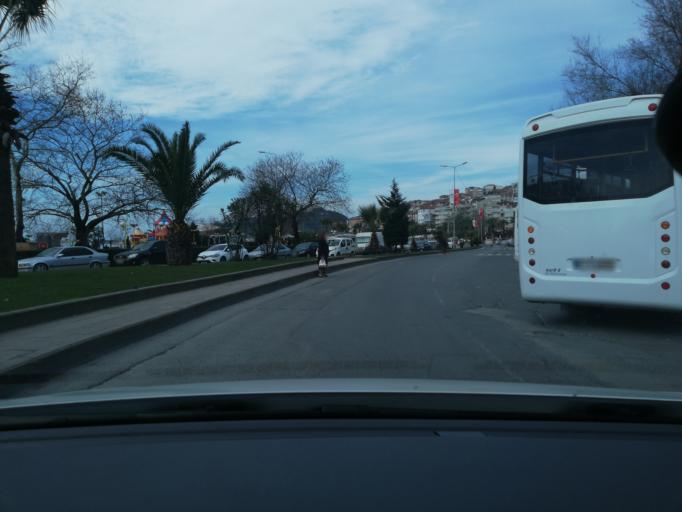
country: TR
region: Zonguldak
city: Eregli
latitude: 41.2781
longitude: 31.4212
